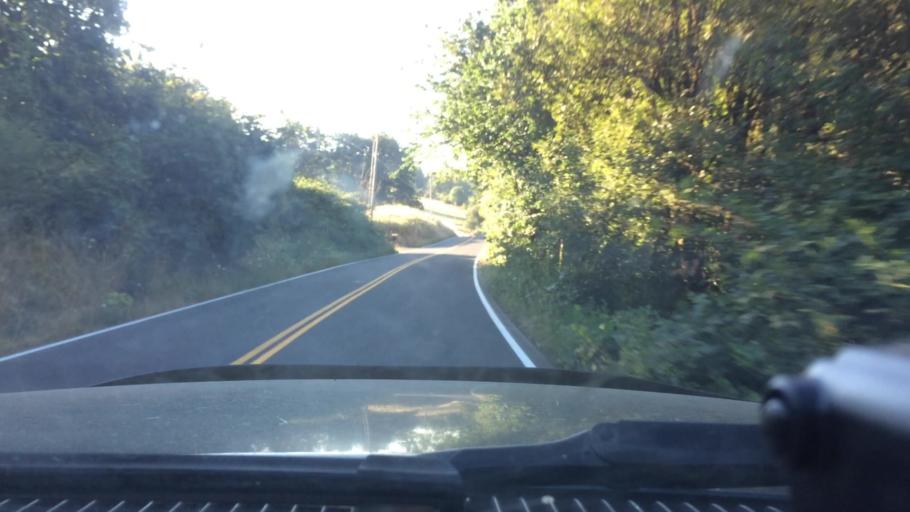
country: US
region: Oregon
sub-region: Yamhill County
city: Newberg
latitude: 45.3426
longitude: -122.9550
